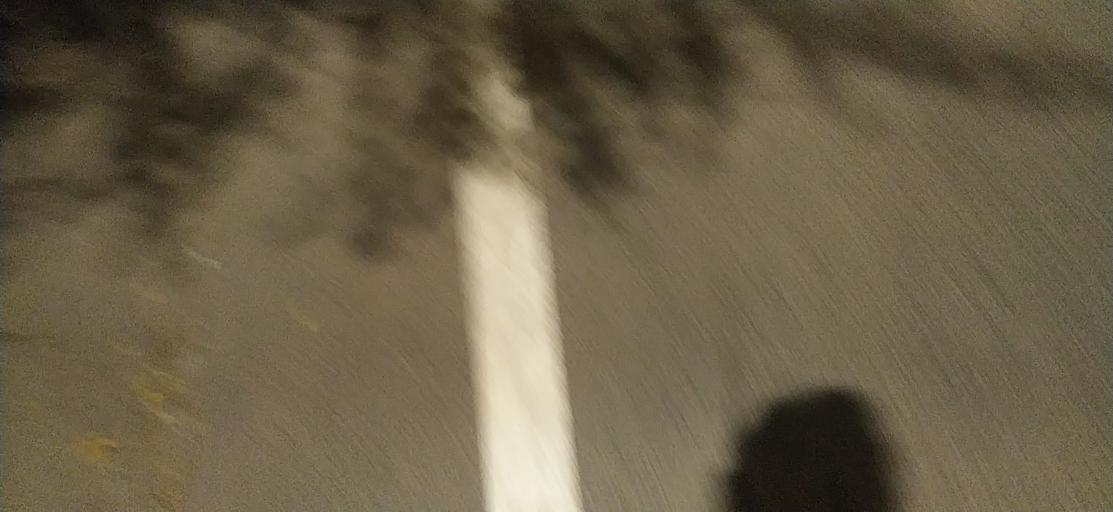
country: IN
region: Uttar Pradesh
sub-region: Ghaziabad
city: Loni
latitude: 28.7016
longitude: 77.2821
